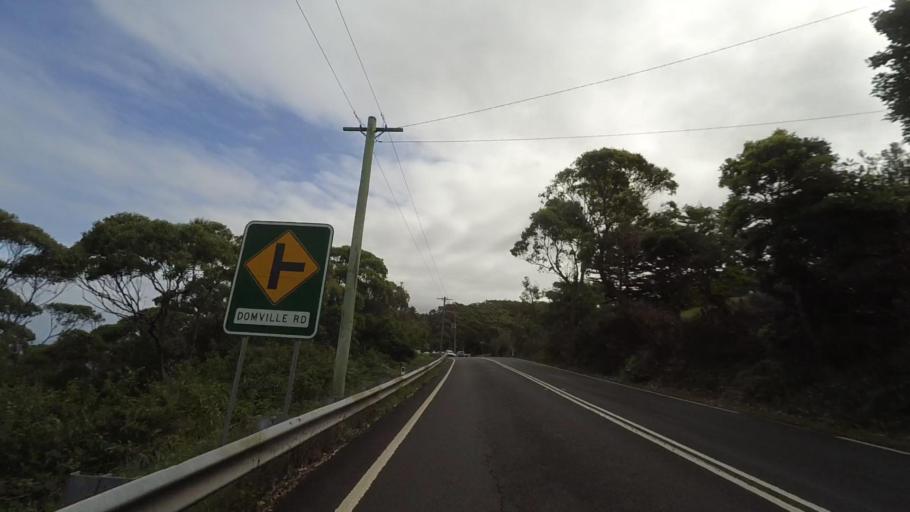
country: AU
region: New South Wales
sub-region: Wollongong
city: Helensburgh
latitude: -34.2133
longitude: 151.0074
